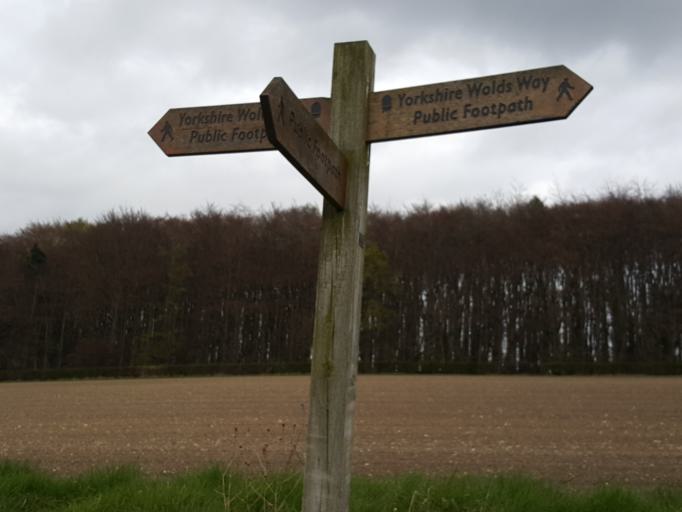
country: GB
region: England
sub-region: East Riding of Yorkshire
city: South Cave
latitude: 53.7705
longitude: -0.5861
